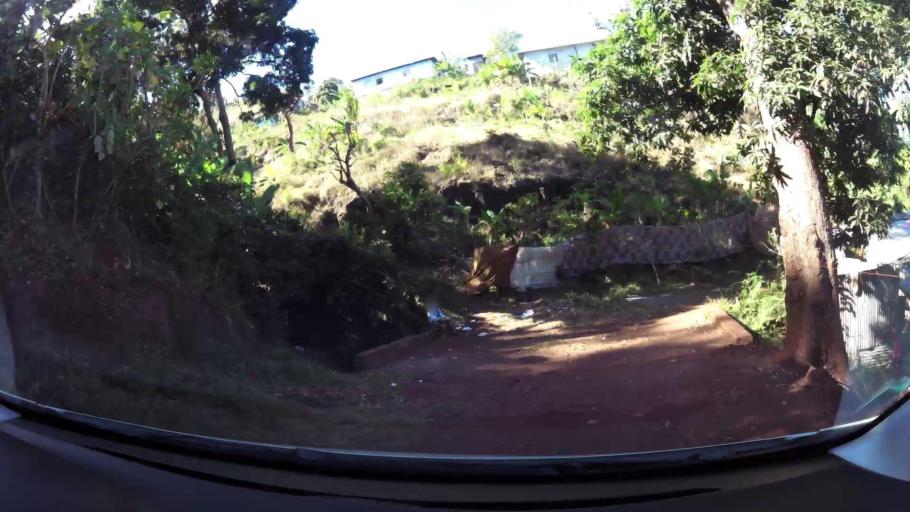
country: YT
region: Mamoudzou
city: Mamoudzou
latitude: -12.7807
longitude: 45.2173
